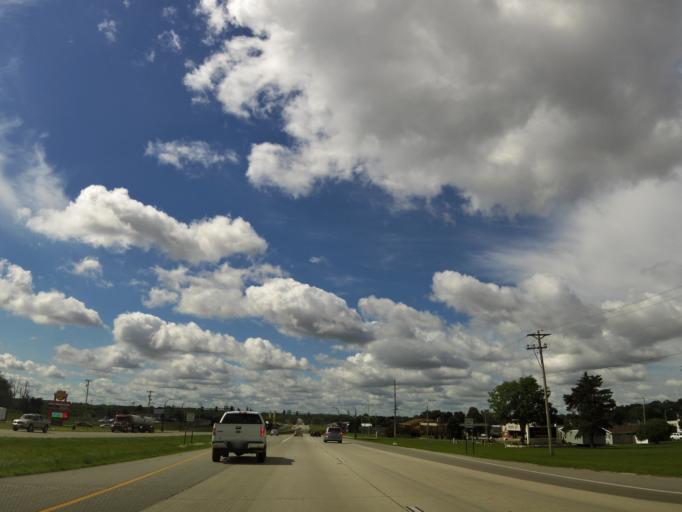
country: US
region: Minnesota
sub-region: Olmsted County
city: Stewartville
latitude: 43.8714
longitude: -92.4885
